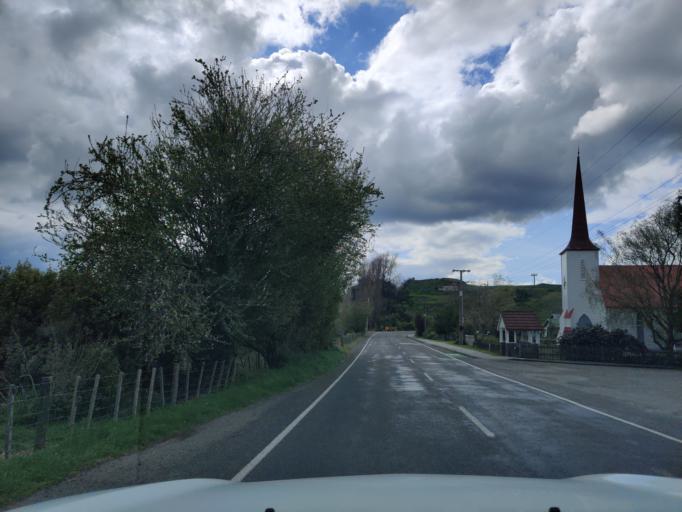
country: NZ
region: Manawatu-Wanganui
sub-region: Wanganui District
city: Wanganui
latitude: -39.8662
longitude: 175.1134
